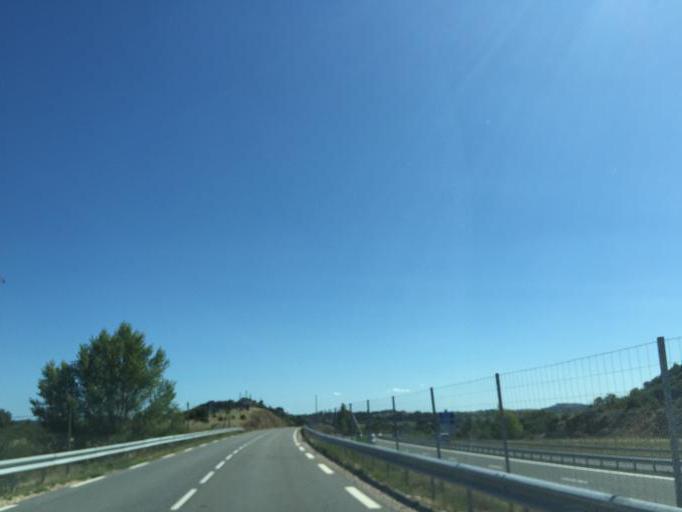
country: FR
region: Languedoc-Roussillon
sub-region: Departement de l'Herault
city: Lodeve
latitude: 43.8785
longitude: 3.3121
